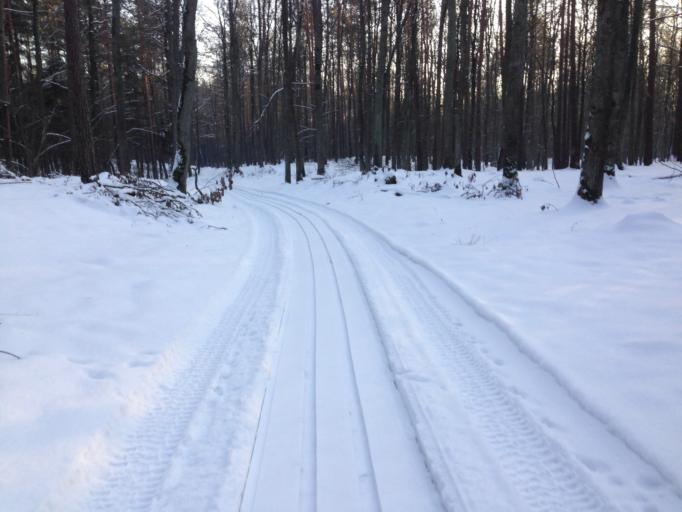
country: PL
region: Kujawsko-Pomorskie
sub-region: Powiat brodnicki
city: Gorzno
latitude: 53.1963
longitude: 19.6699
